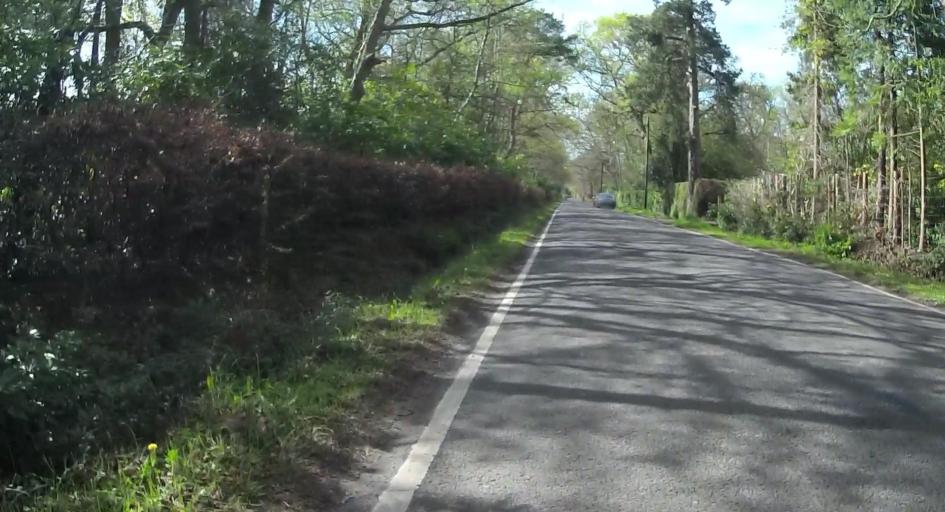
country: GB
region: England
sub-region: Surrey
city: Farnham
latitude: 51.1809
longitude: -0.8145
